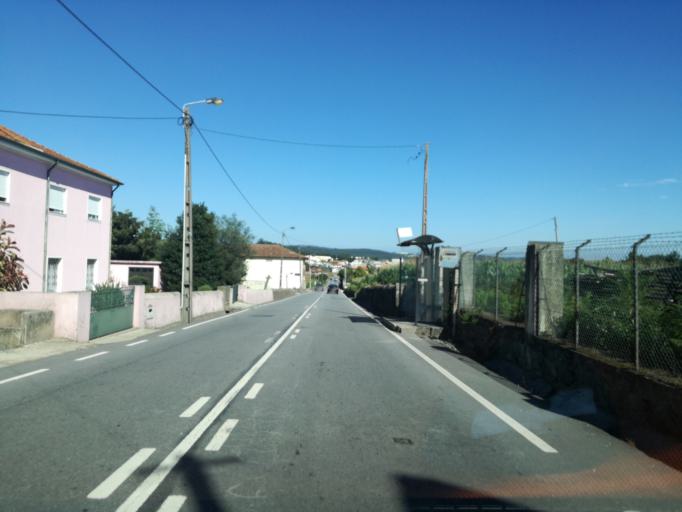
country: PT
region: Porto
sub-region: Trofa
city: Sao Romao do Coronado
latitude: 41.2837
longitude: -8.5743
